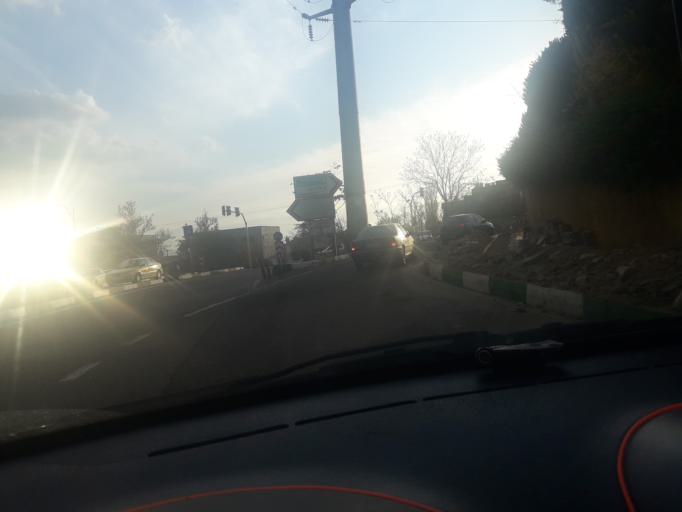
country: IR
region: Tehran
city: Tehran
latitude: 35.7449
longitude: 51.3979
